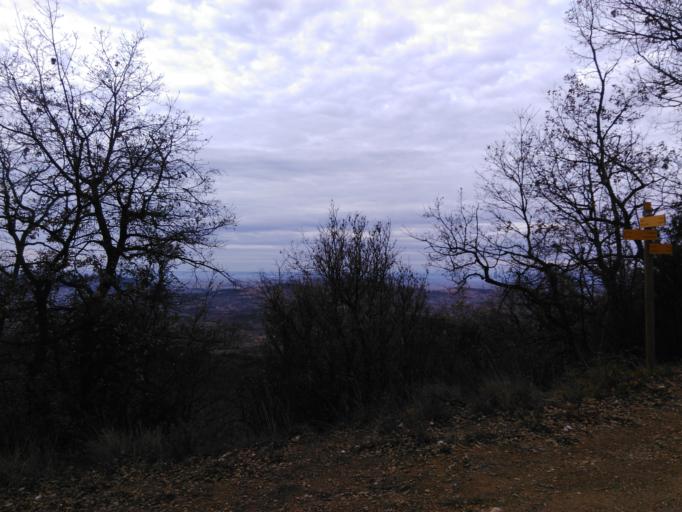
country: FR
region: Rhone-Alpes
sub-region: Departement de la Drome
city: Mirabel-aux-Baronnies
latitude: 44.2966
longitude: 5.1675
